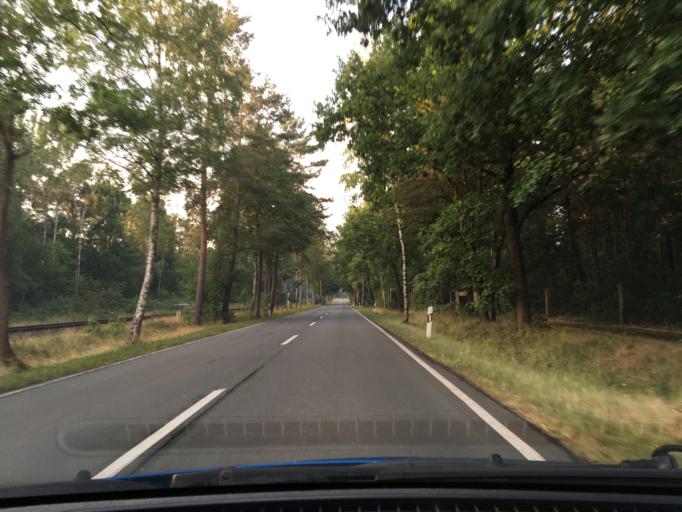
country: DE
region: Lower Saxony
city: Celle
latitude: 52.7079
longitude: 10.0810
